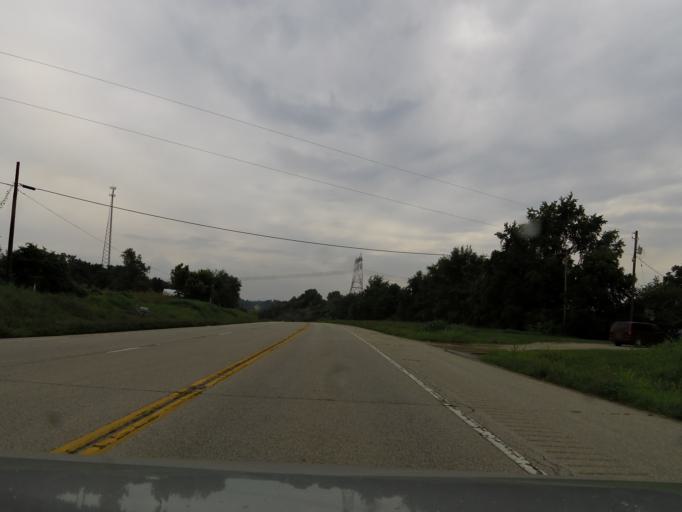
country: US
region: Ohio
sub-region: Brown County
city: Aberdeen
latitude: 38.5811
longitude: -83.8287
